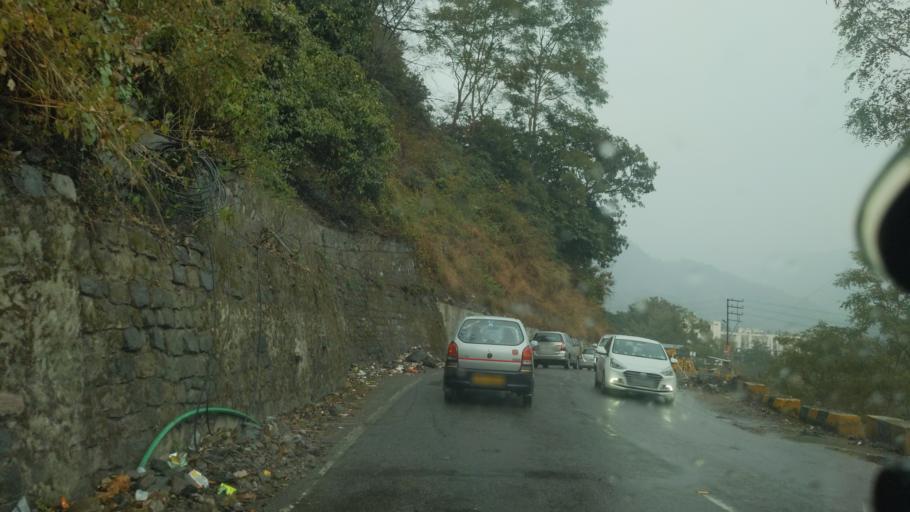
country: IN
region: Uttarakhand
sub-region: Naini Tal
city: Haldwani
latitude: 29.2794
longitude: 79.5448
